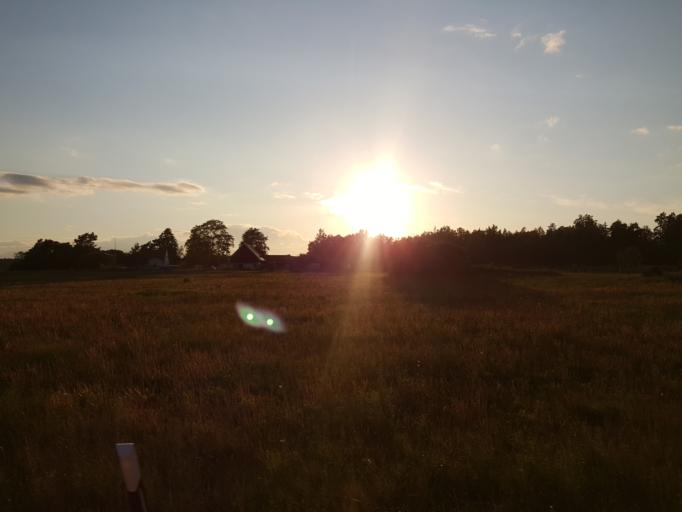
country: SE
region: Uppsala
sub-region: Uppsala Kommun
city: Storvreta
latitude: 59.8986
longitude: 17.7095
